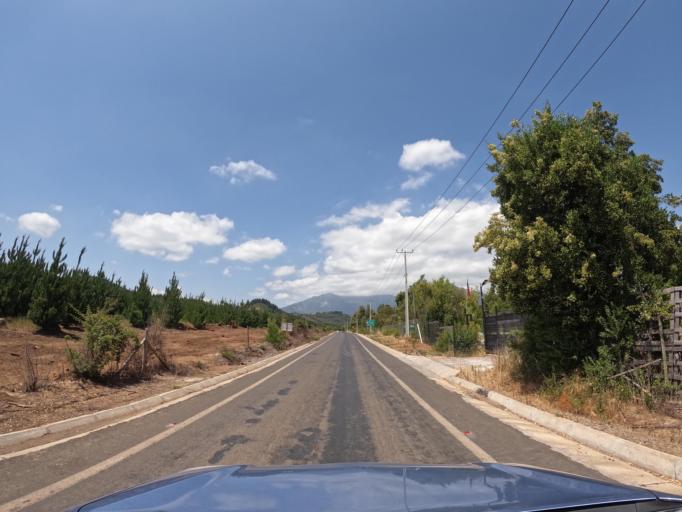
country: CL
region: Maule
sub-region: Provincia de Curico
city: Molina
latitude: -35.1783
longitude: -71.1082
